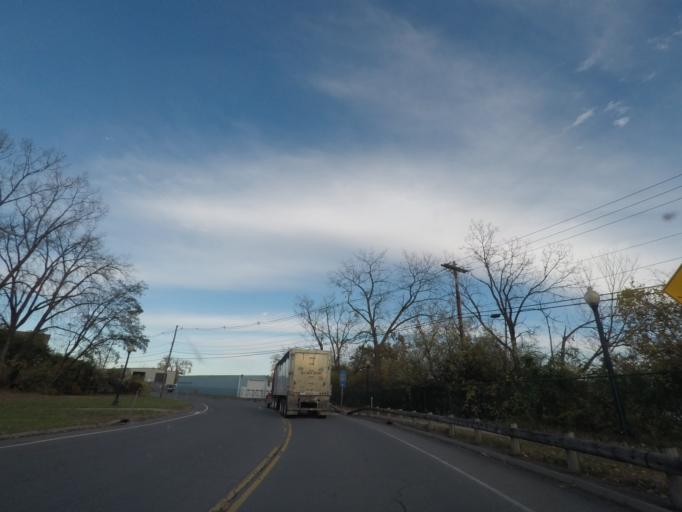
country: US
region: New York
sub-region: Rensselaer County
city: Rensselaer
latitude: 42.6363
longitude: -73.7545
